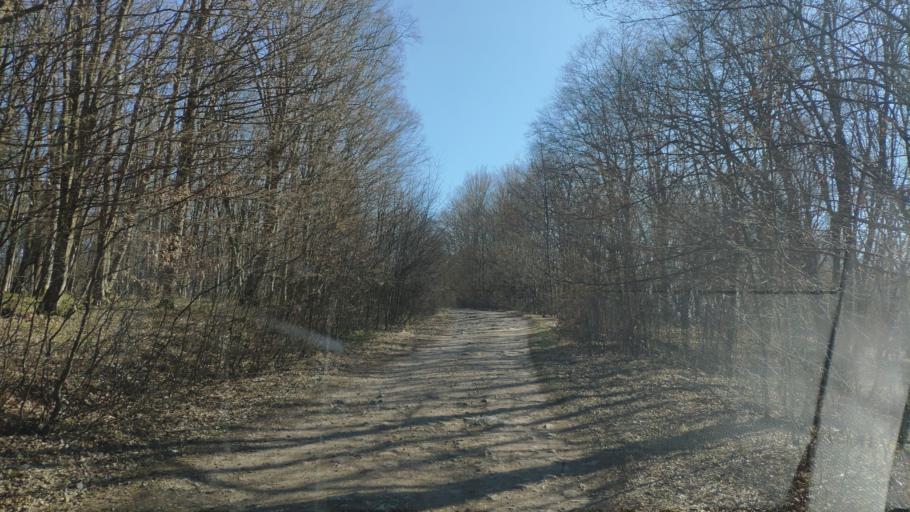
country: SK
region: Kosicky
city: Roznava
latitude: 48.5987
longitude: 20.4108
